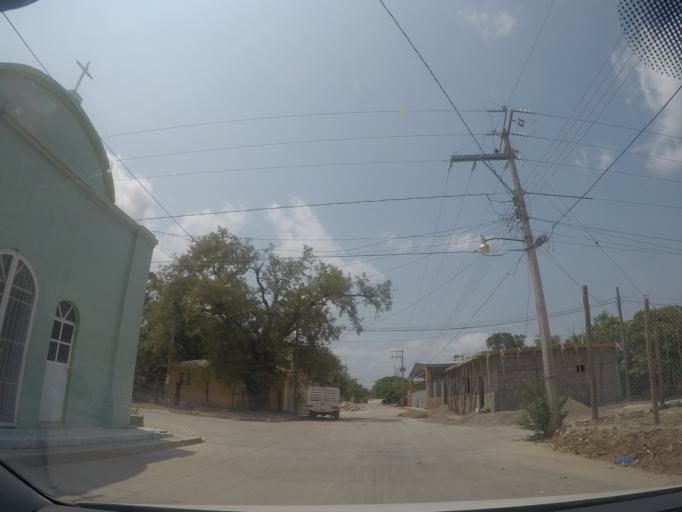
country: MX
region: Oaxaca
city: Asuncion Ixtaltepec
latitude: 16.5066
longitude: -95.0627
